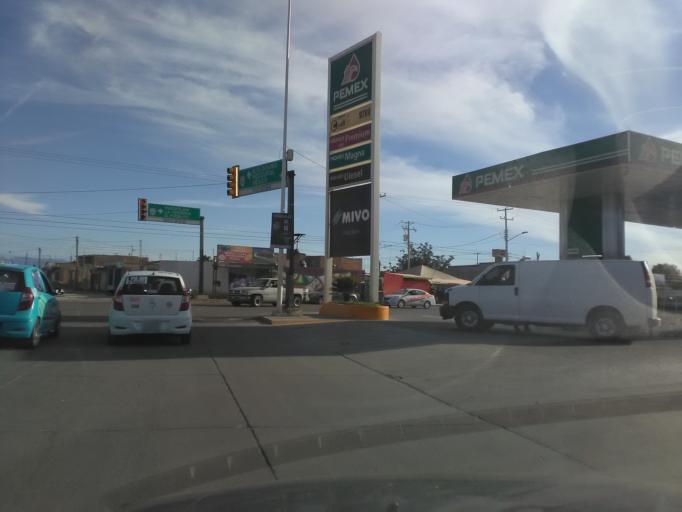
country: MX
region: Durango
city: Victoria de Durango
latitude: 24.0125
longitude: -104.6225
